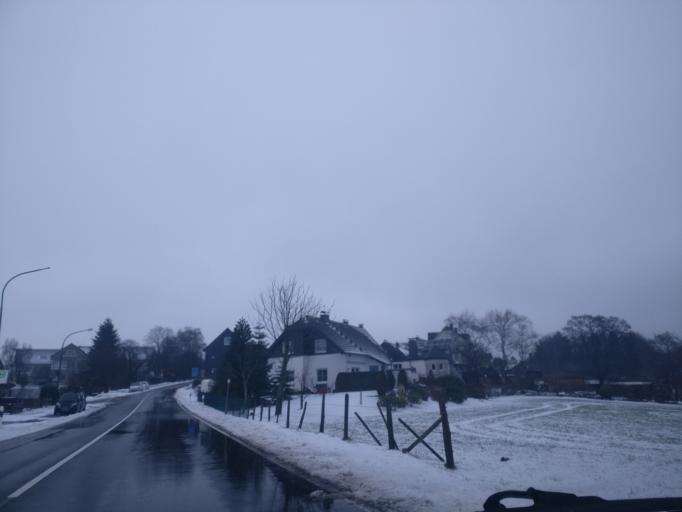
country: DE
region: North Rhine-Westphalia
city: Radevormwald
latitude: 51.1965
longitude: 7.3338
